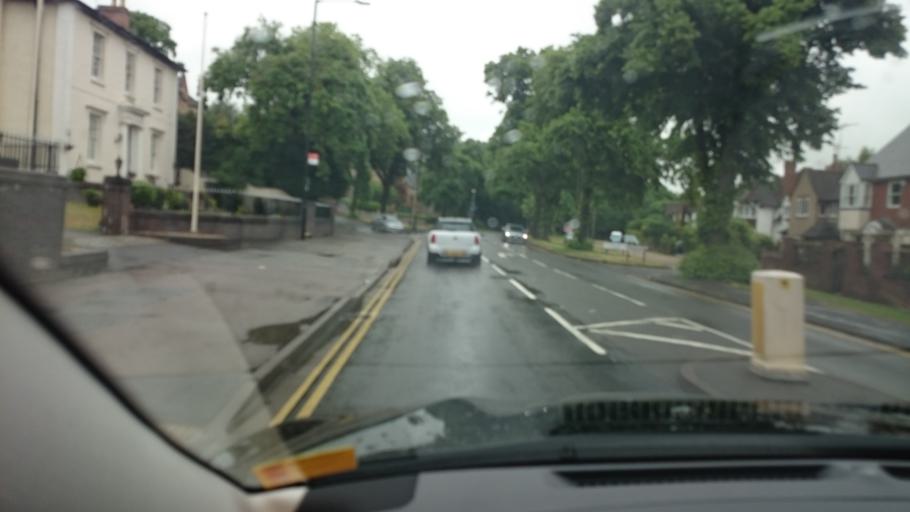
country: GB
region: England
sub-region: Warwickshire
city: Stratford-upon-Avon
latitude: 52.1954
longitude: -1.7022
